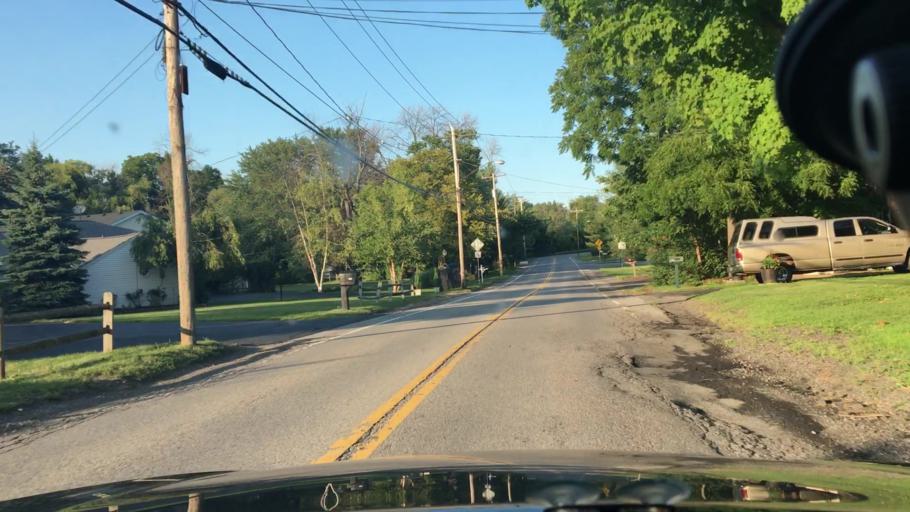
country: US
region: New York
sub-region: Erie County
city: Amherst
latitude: 42.9807
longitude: -78.7687
